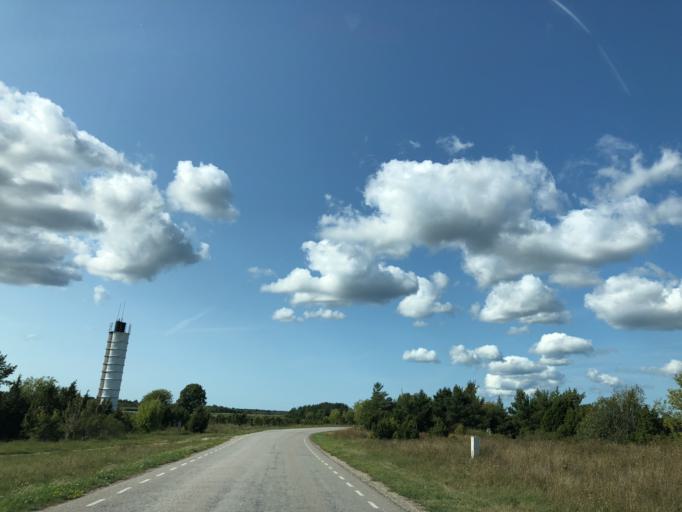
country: EE
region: Hiiumaa
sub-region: Kaerdla linn
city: Kardla
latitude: 58.7898
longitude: 22.7723
